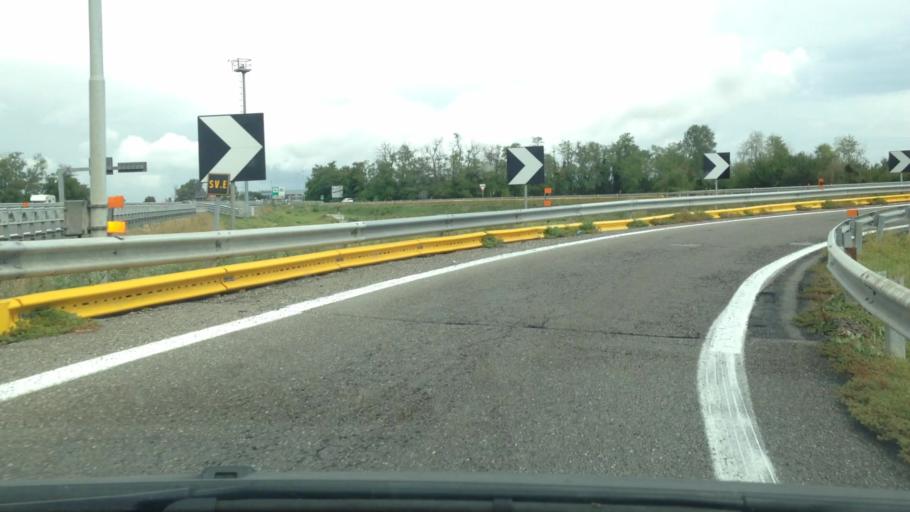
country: IT
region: Piedmont
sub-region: Provincia di Alessandria
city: Tortona
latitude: 44.9229
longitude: 8.8462
